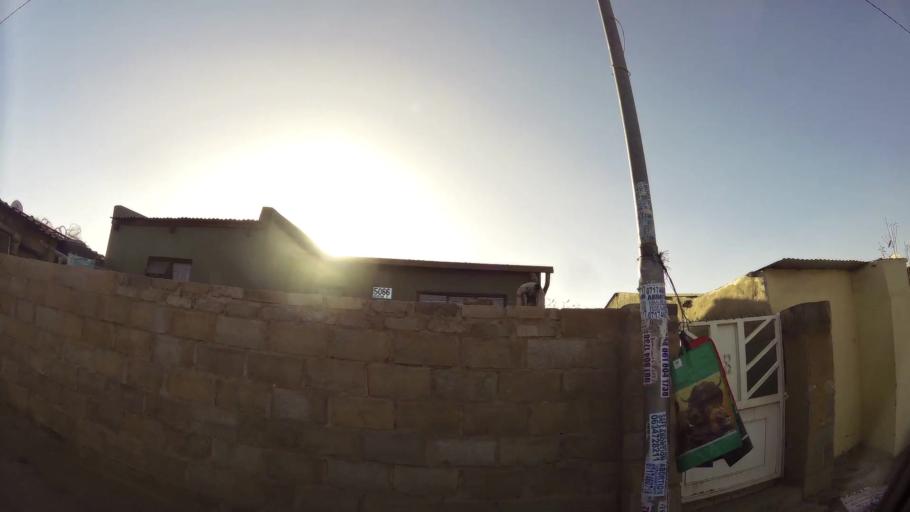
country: ZA
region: Gauteng
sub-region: City of Johannesburg Metropolitan Municipality
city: Diepsloot
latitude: -25.9238
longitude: 28.0117
